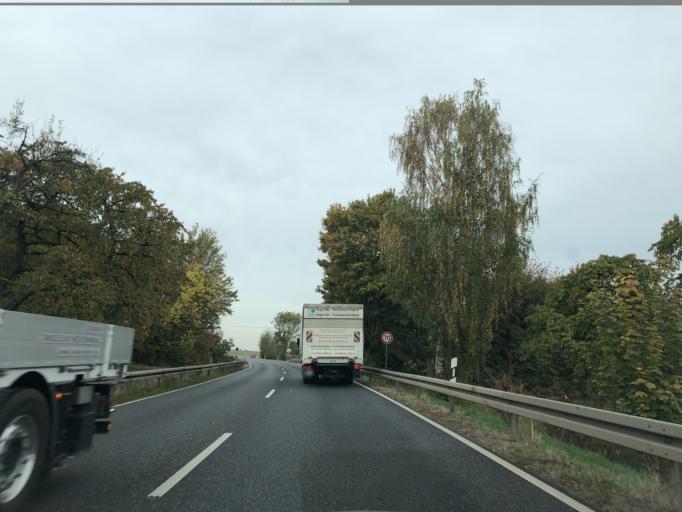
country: DE
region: Hesse
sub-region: Regierungsbezirk Darmstadt
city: Niederdorfelden
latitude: 50.1893
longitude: 8.7818
